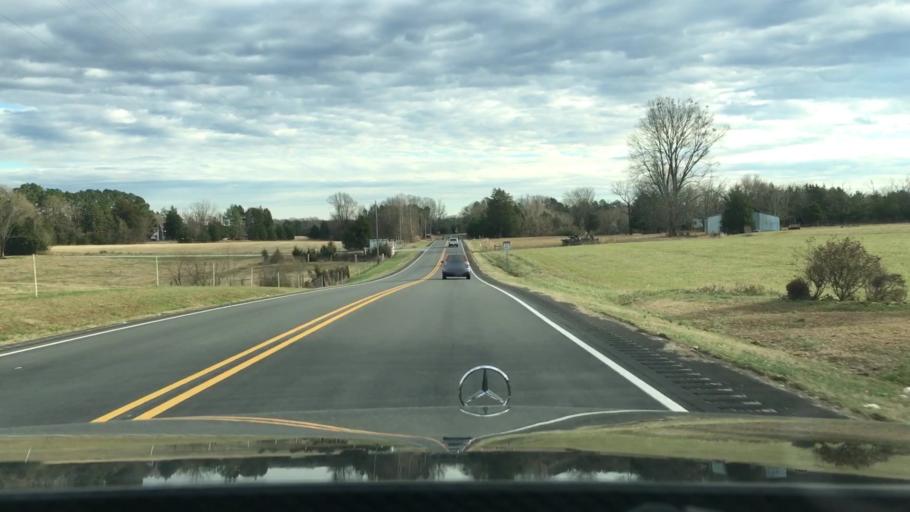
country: US
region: North Carolina
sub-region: Caswell County
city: Yanceyville
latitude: 36.3690
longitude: -79.2563
